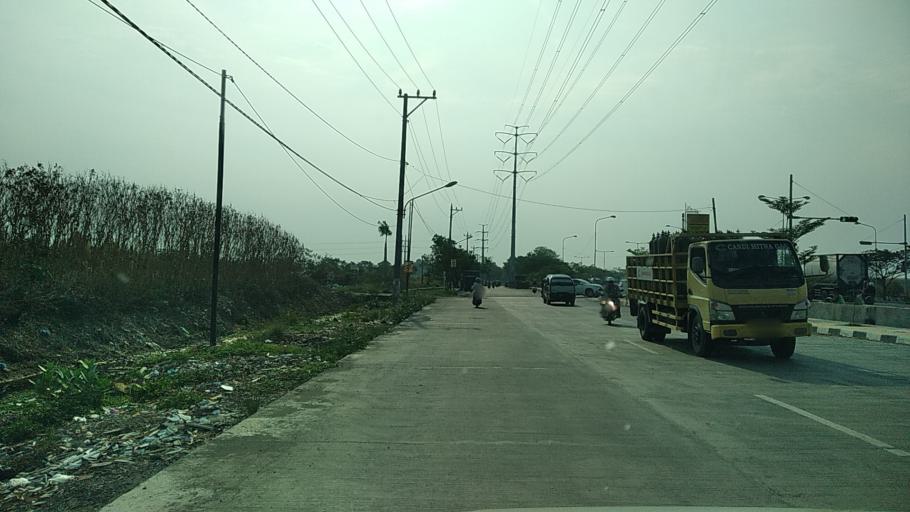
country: ID
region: Central Java
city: Semarang
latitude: -6.9543
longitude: 110.4036
